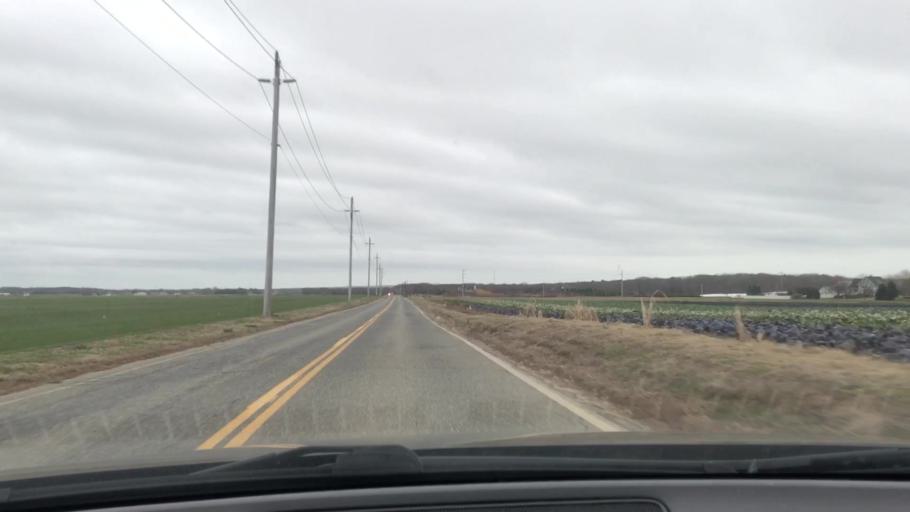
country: US
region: New York
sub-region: Suffolk County
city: Riverhead
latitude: 40.9639
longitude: -72.6724
